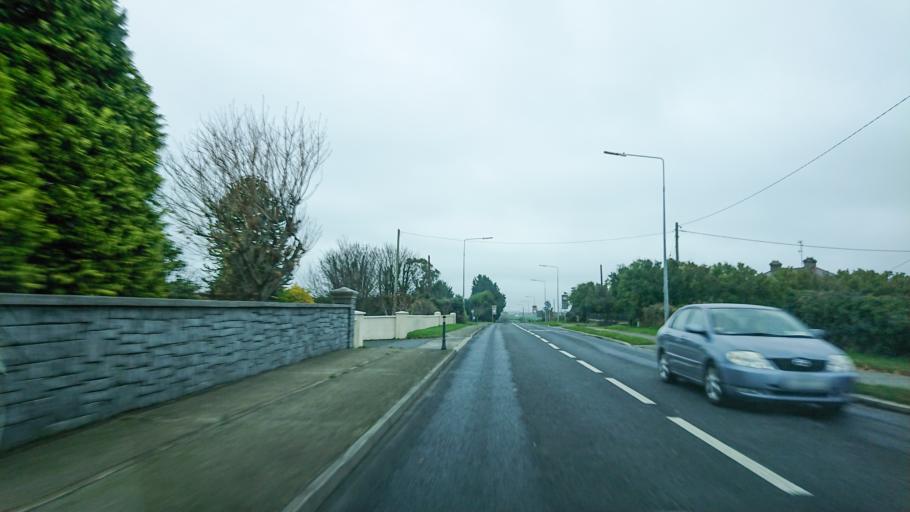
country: IE
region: Leinster
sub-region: Kilkenny
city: Mooncoin
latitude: 52.2909
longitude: -7.2463
